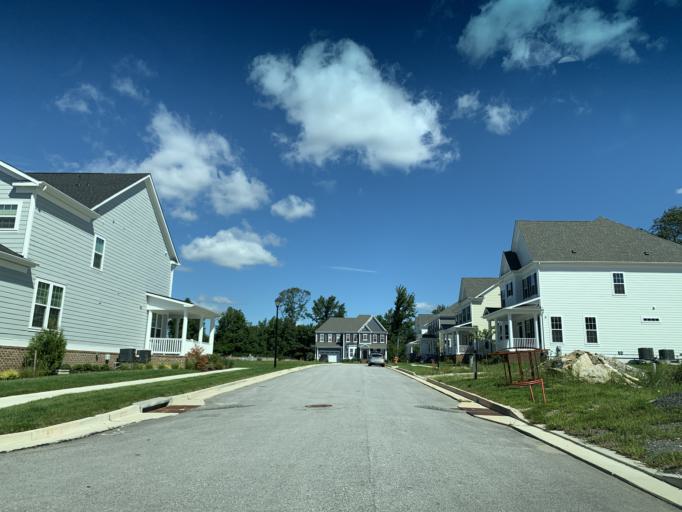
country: US
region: Maryland
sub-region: Baltimore County
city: Bowleys Quarters
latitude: 39.3625
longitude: -76.4021
